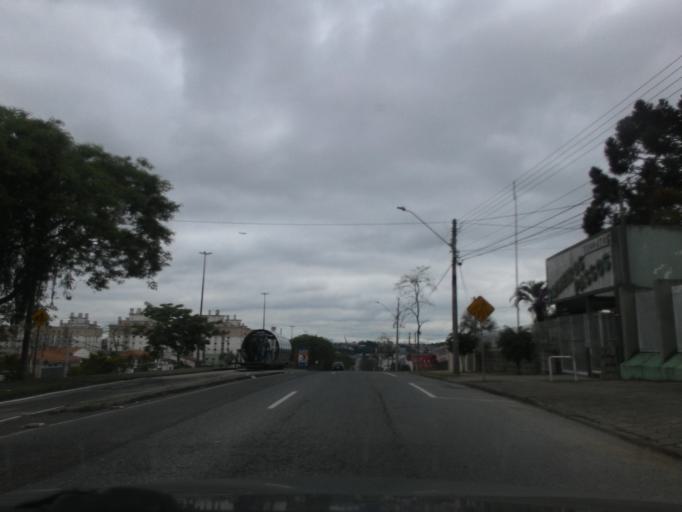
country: BR
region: Parana
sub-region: Curitiba
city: Curitiba
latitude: -25.4742
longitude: -49.2704
